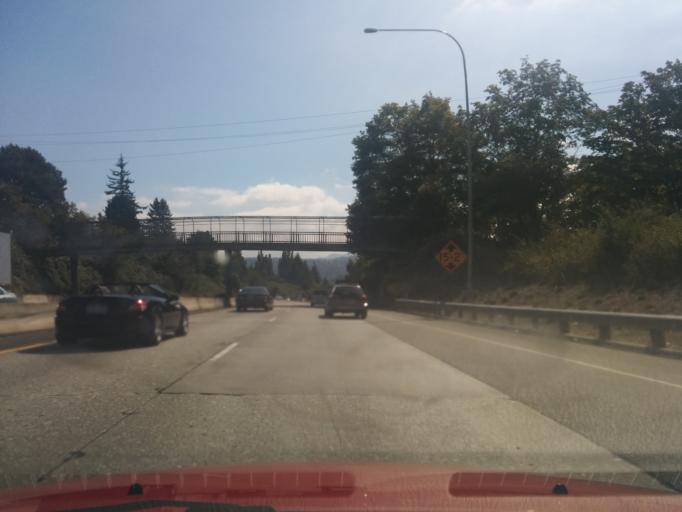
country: US
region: Washington
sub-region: Whatcom County
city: Bellingham
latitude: 48.7685
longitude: -122.4626
